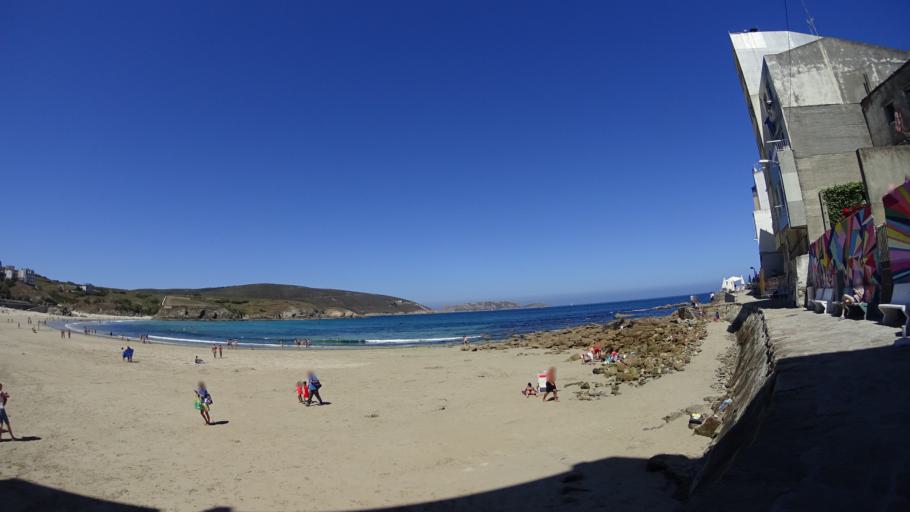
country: ES
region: Galicia
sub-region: Provincia da Coruna
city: Malpica
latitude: 43.3235
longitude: -8.8113
